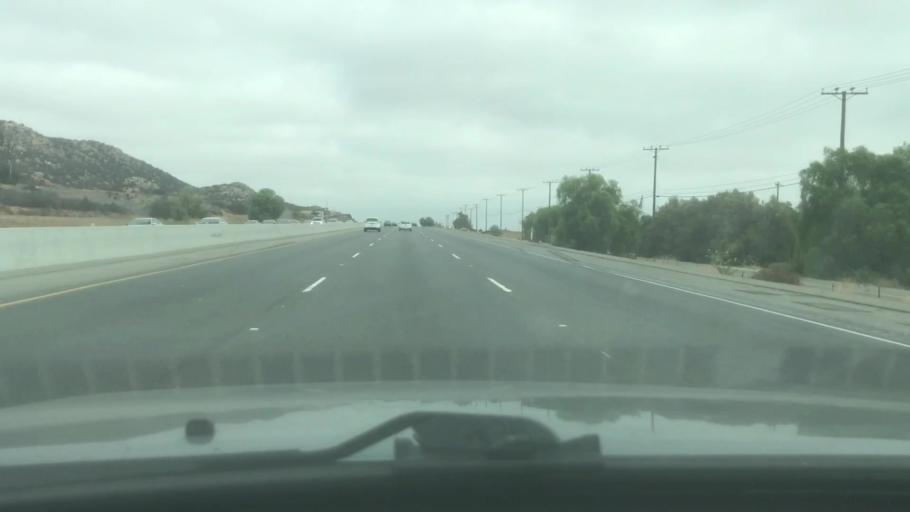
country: US
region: California
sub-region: Riverside County
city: Murrieta Hot Springs
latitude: 33.6078
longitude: -117.1708
